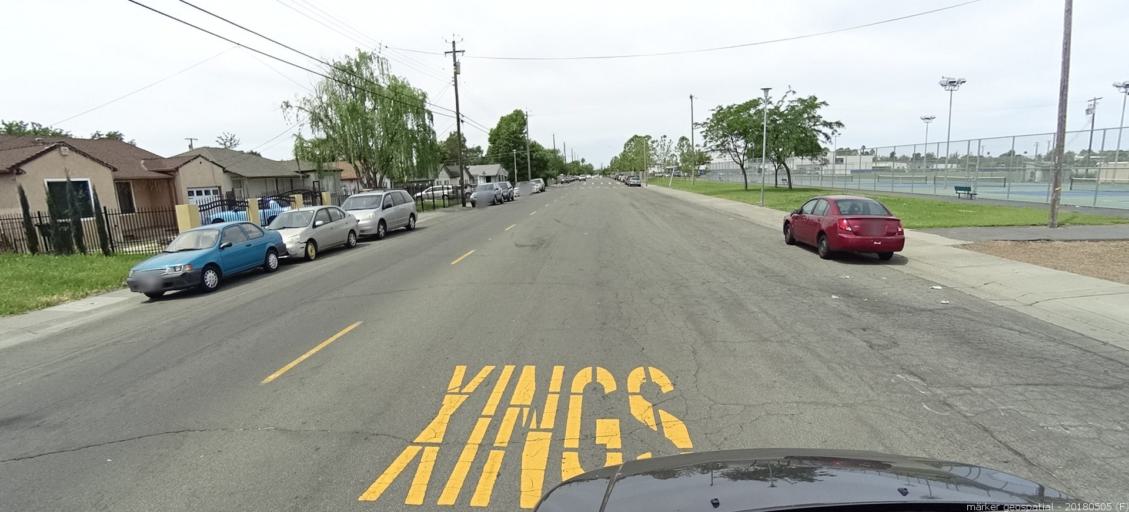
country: US
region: California
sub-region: Sacramento County
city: Rio Linda
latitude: 38.6330
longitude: -121.4339
